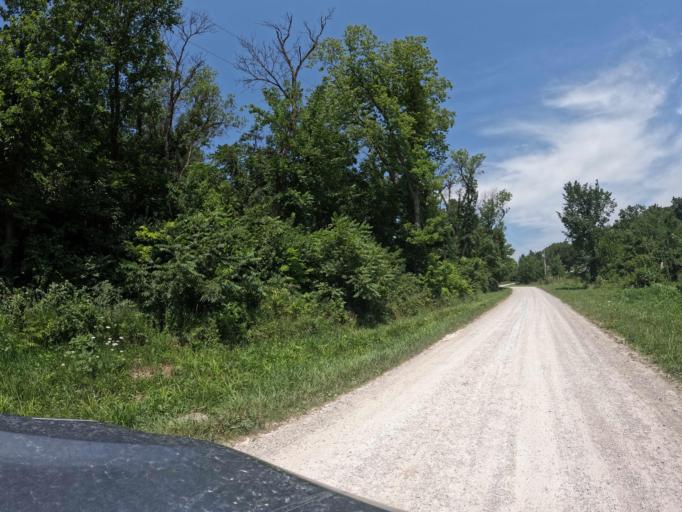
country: US
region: Iowa
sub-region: Appanoose County
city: Centerville
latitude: 40.7777
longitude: -92.9506
